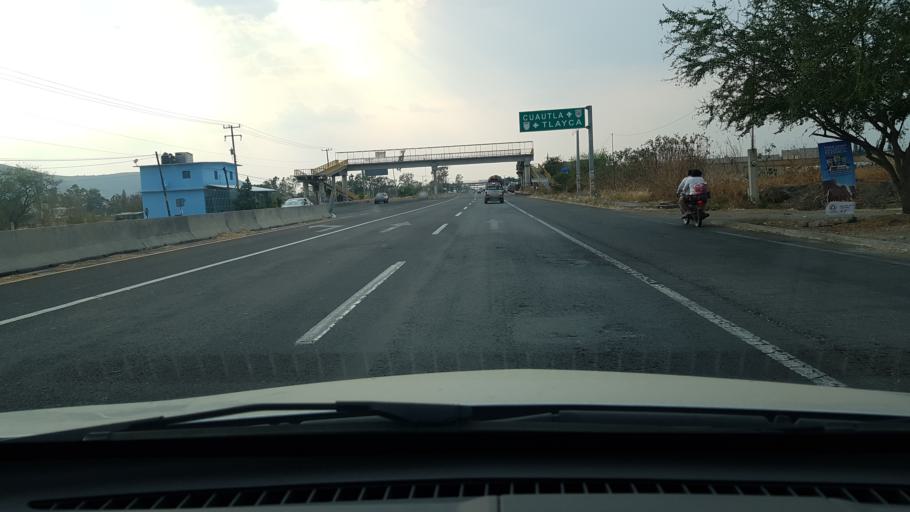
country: MX
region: Morelos
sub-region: Ayala
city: Unidad Habitacional Mariano Matamoros
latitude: 18.7430
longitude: -98.8358
